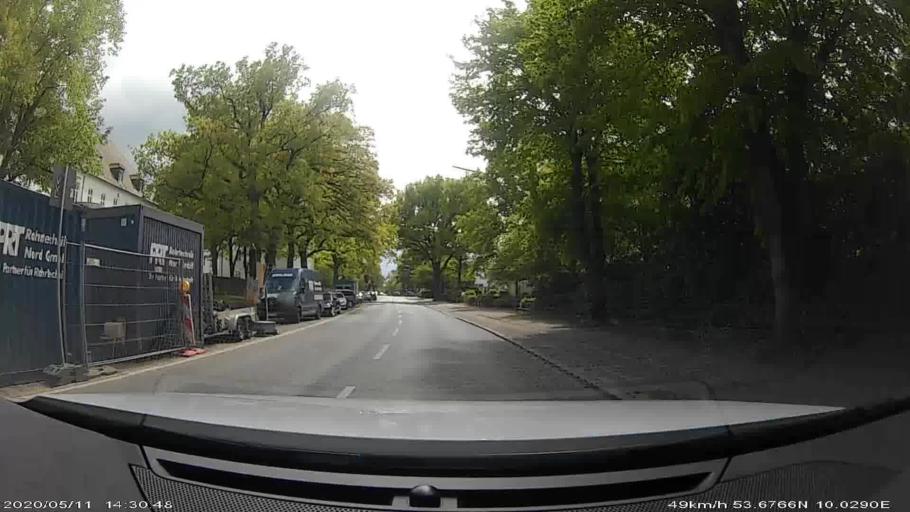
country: DE
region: Hamburg
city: Langenhorn
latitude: 53.6667
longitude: 10.0246
